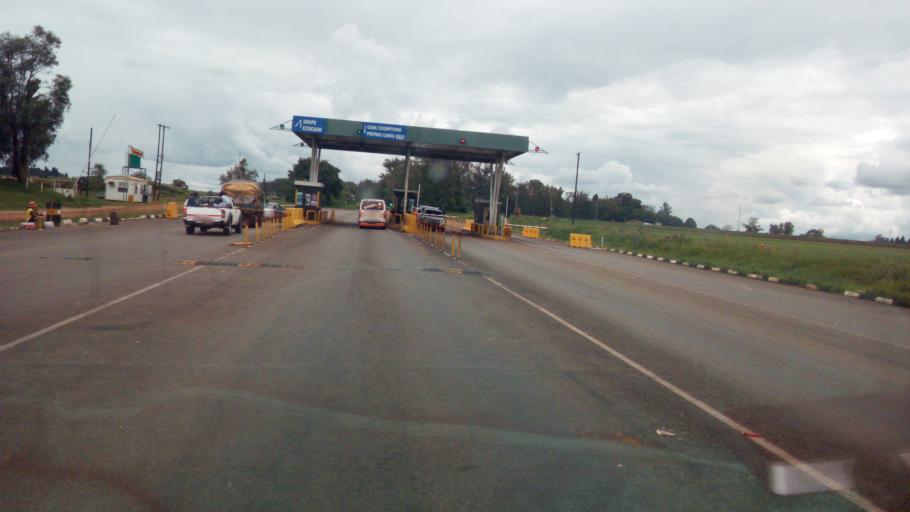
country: ZW
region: Harare
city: Harare
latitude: -17.6922
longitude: 31.0078
